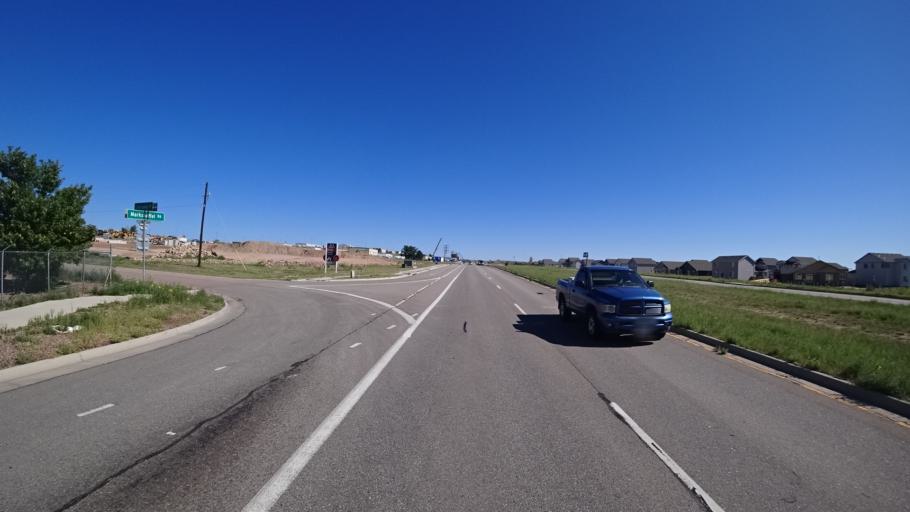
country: US
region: Colorado
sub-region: El Paso County
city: Cimarron Hills
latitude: 38.8736
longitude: -104.6829
